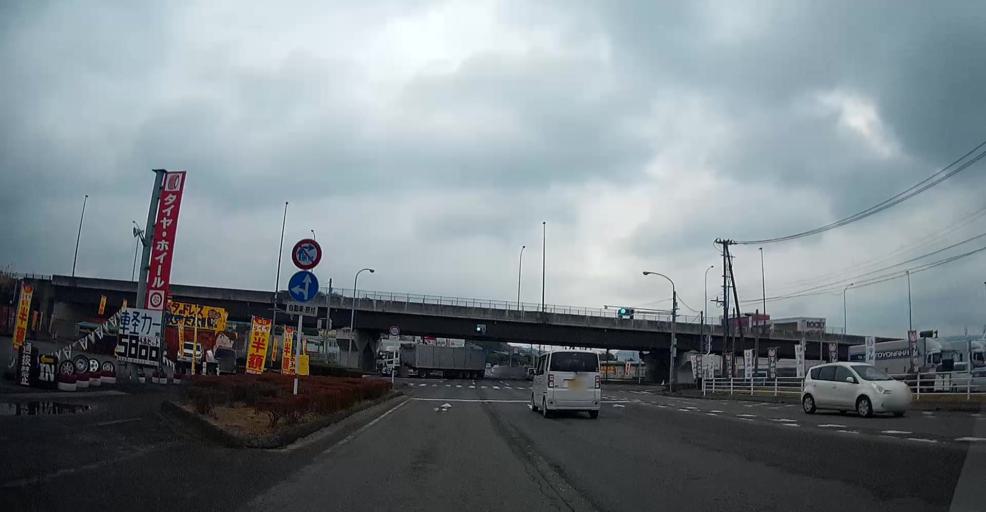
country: JP
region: Kumamoto
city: Matsubase
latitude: 32.6517
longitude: 130.6990
